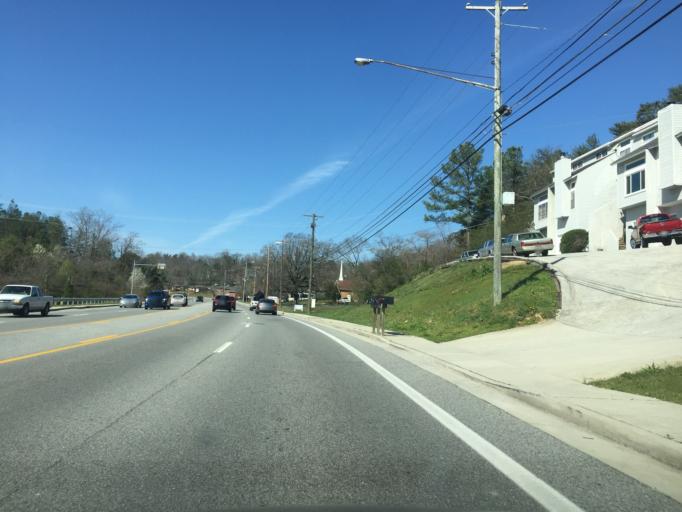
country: US
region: Tennessee
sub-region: Hamilton County
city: Red Bank
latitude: 35.1168
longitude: -85.2643
